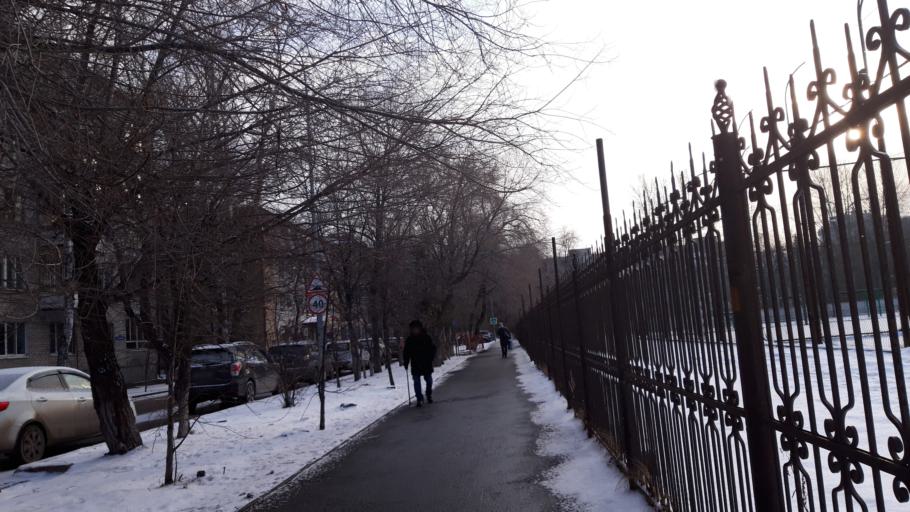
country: RU
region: Tjumen
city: Tyumen
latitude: 57.1523
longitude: 65.5484
